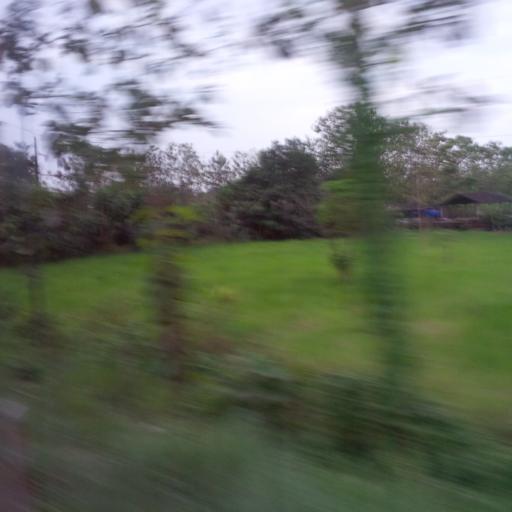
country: EC
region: Canar
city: La Troncal
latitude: -2.3422
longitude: -79.3769
